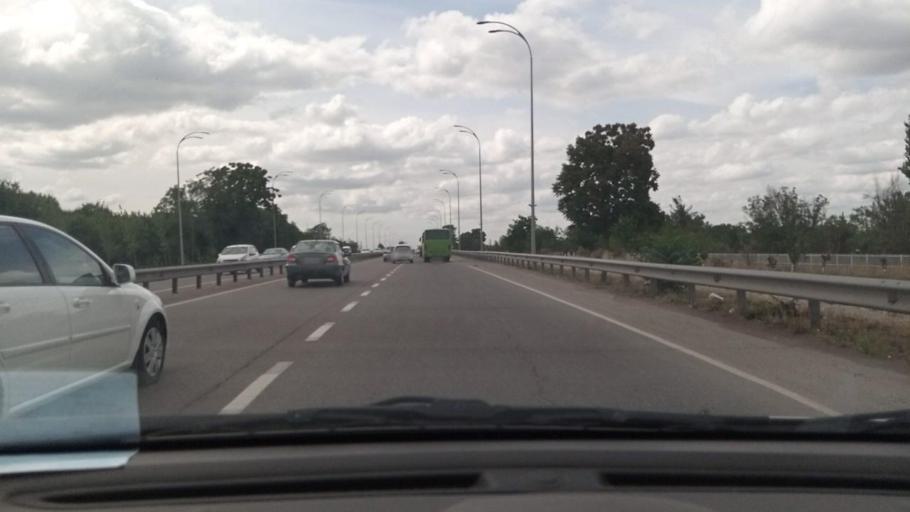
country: UZ
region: Toshkent Shahri
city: Bektemir
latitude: 41.2588
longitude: 69.3783
